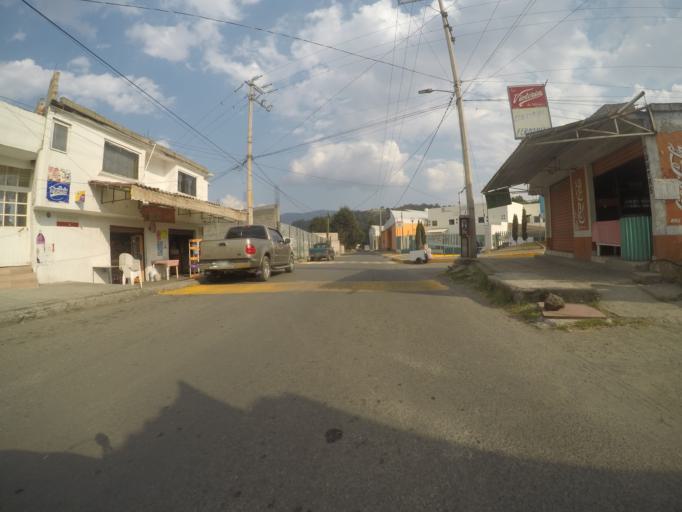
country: MX
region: Mexico
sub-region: Xalatlaco
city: Techichili
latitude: 19.1728
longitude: -99.4185
